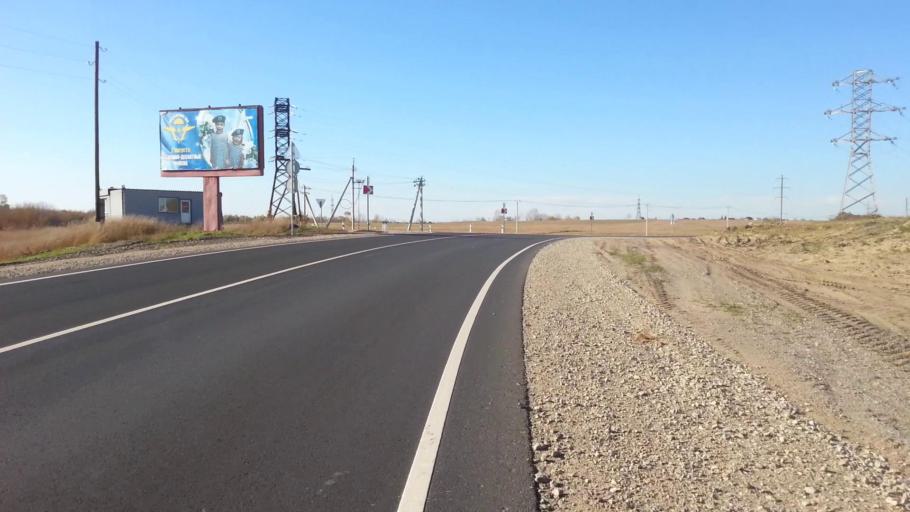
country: RU
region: Altai Krai
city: Sannikovo
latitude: 53.3289
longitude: 83.9396
